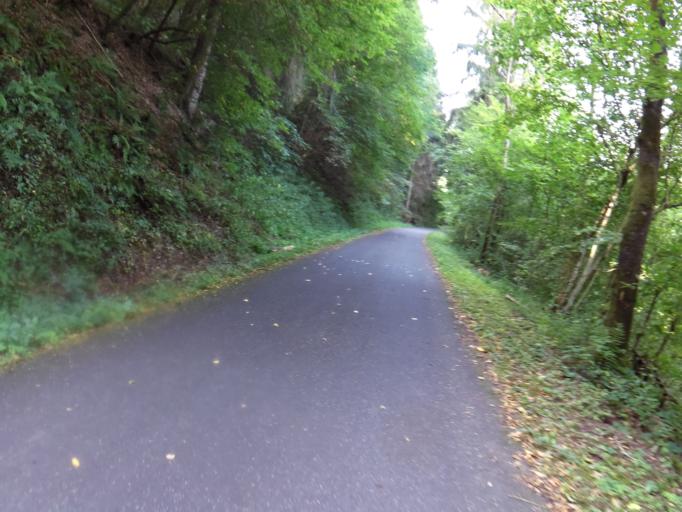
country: DE
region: Rheinland-Pfalz
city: Preist
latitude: 49.9216
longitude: 6.6178
